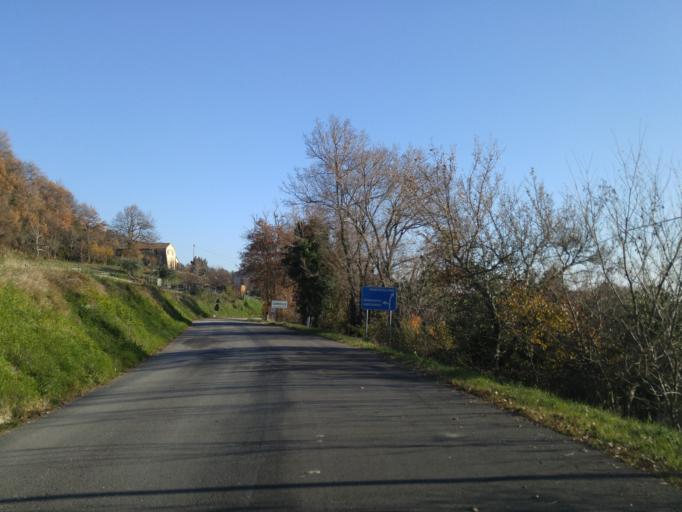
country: IT
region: The Marches
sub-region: Provincia di Pesaro e Urbino
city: Isola del Piano
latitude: 43.7675
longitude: 12.7999
